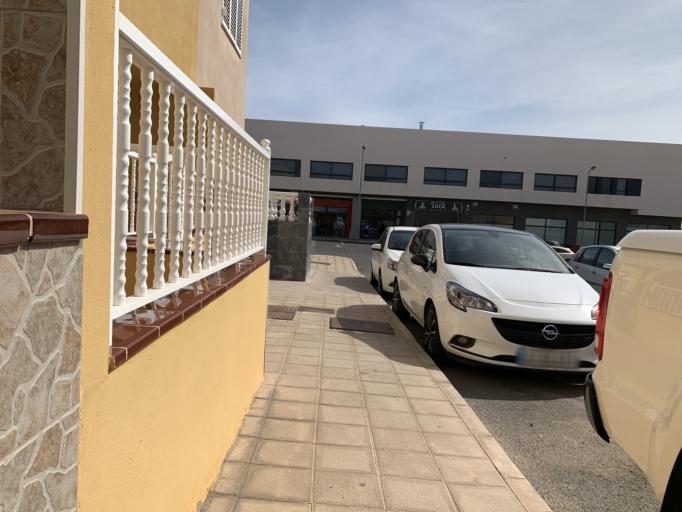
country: ES
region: Canary Islands
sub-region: Provincia de Las Palmas
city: Puerto del Rosario
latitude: 28.5104
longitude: -13.8600
